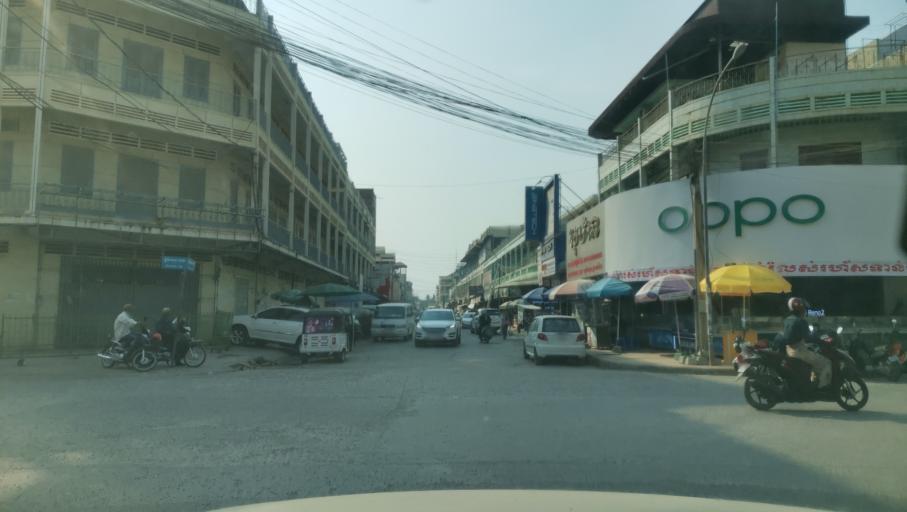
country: KH
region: Battambang
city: Battambang
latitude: 13.1041
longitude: 103.1961
